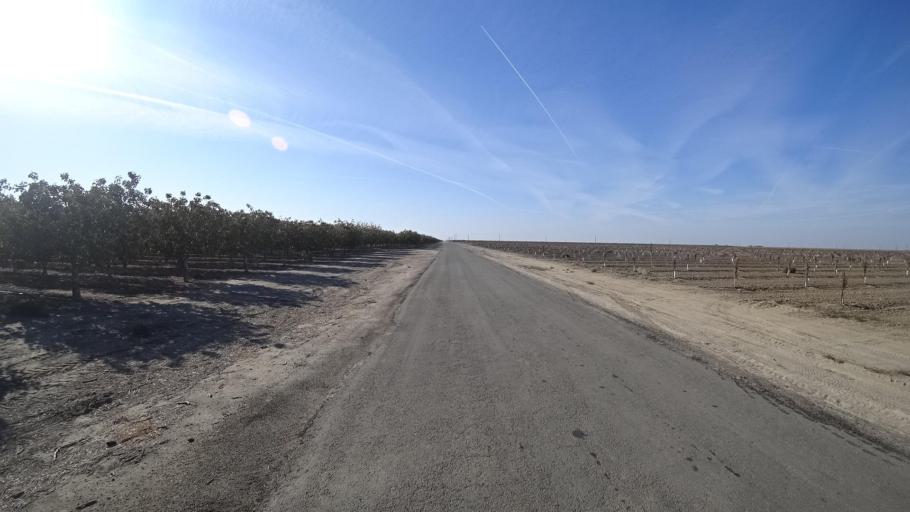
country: US
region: California
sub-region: Kern County
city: Wasco
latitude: 35.6887
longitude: -119.4145
